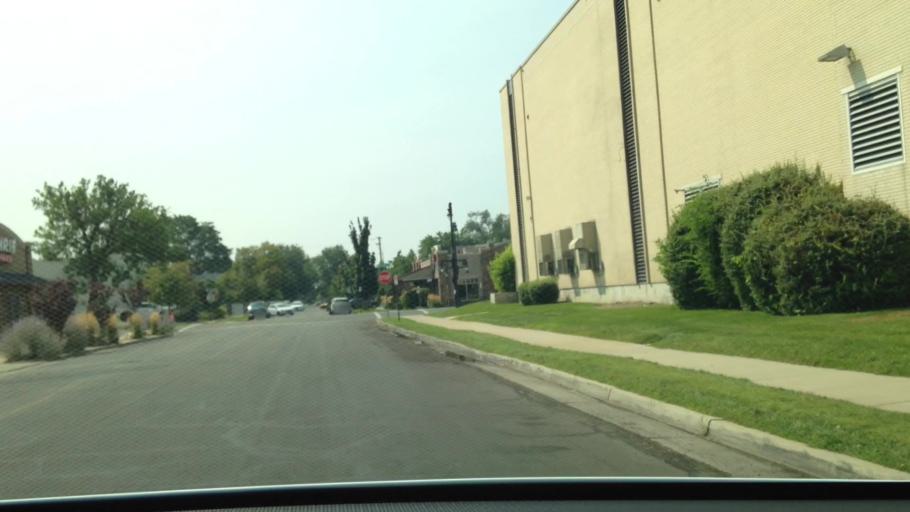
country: US
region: Utah
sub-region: Salt Lake County
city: South Salt Lake
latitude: 40.7261
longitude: -111.8683
